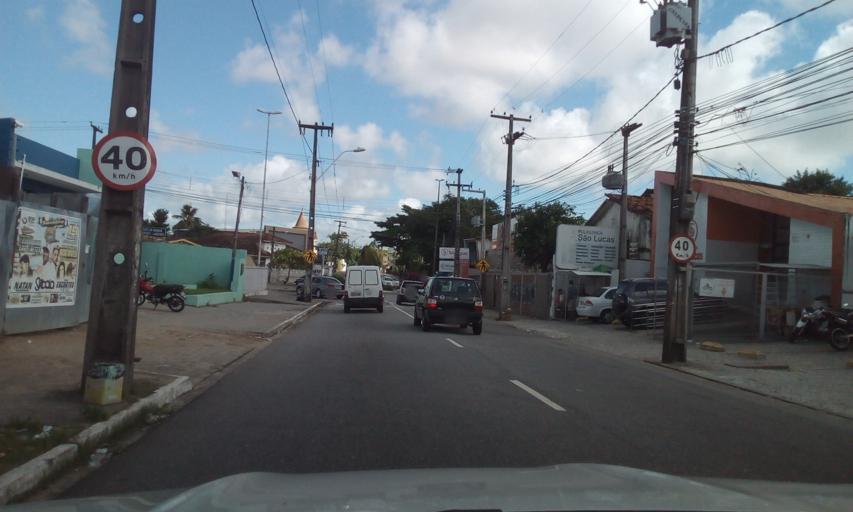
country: BR
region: Paraiba
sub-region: Joao Pessoa
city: Joao Pessoa
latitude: -7.1343
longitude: -34.8819
